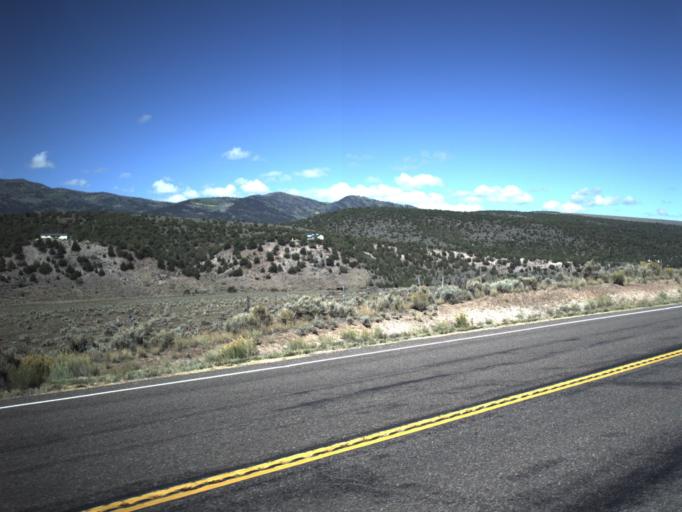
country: US
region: Utah
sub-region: Wayne County
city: Loa
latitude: 38.5695
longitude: -111.8405
